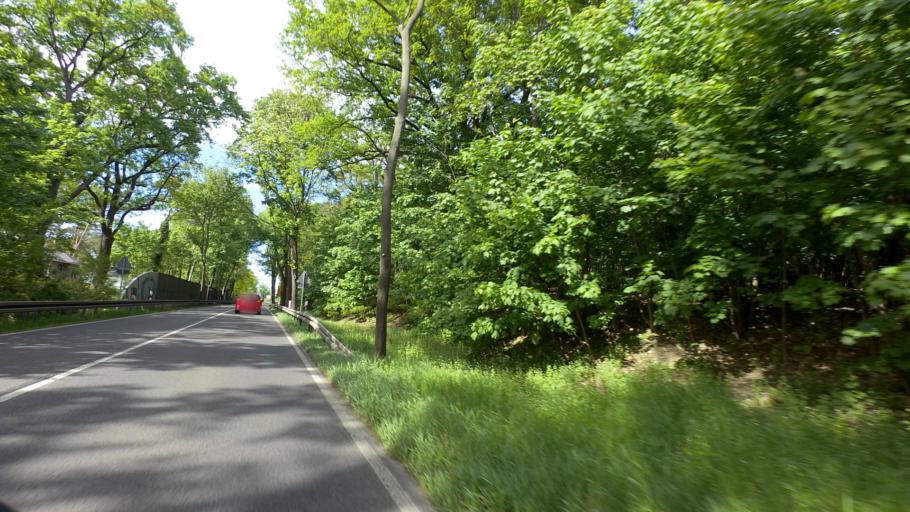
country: DE
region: Brandenburg
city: Rangsdorf
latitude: 52.2924
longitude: 13.4584
